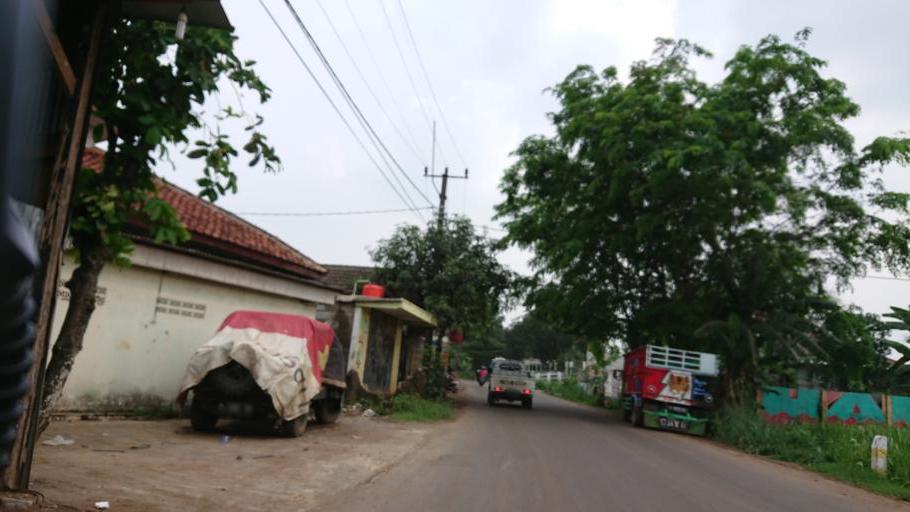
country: ID
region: West Java
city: Parung
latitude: -6.4580
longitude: 106.7055
